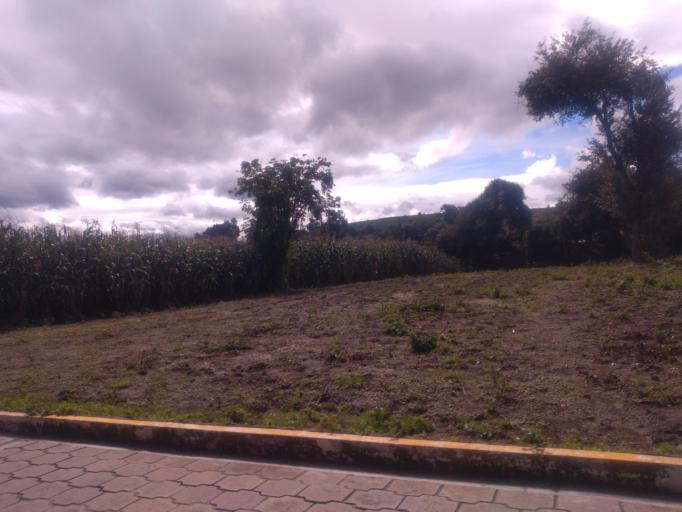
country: GT
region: Quetzaltenango
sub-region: Municipio de La Esperanza
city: La Esperanza
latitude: 14.8553
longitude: -91.5649
